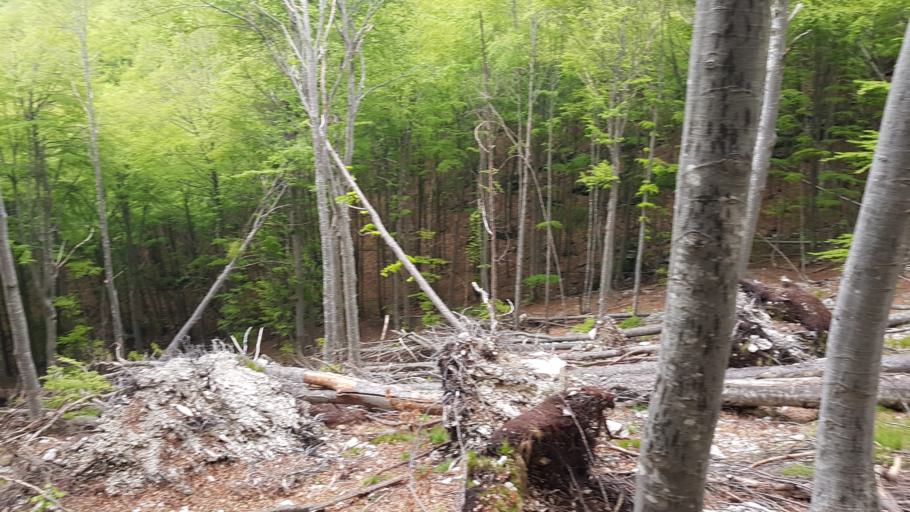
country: IT
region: Friuli Venezia Giulia
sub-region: Provincia di Udine
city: Chiaulis
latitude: 46.3122
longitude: 12.9757
